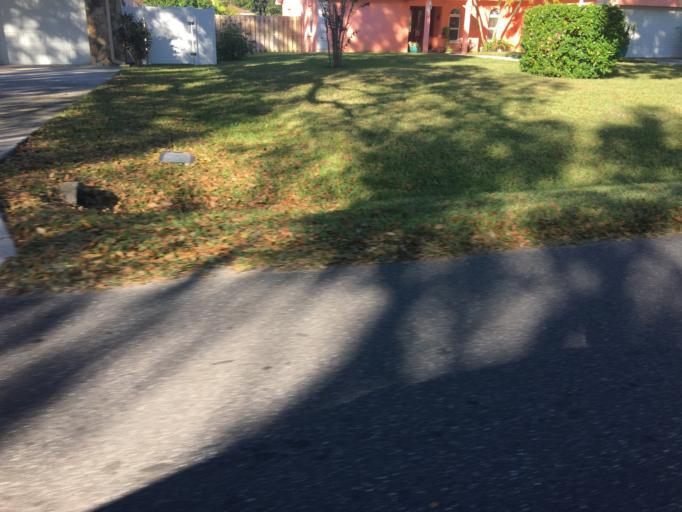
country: US
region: Florida
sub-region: Hillsborough County
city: Egypt Lake-Leto
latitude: 28.0181
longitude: -82.4983
